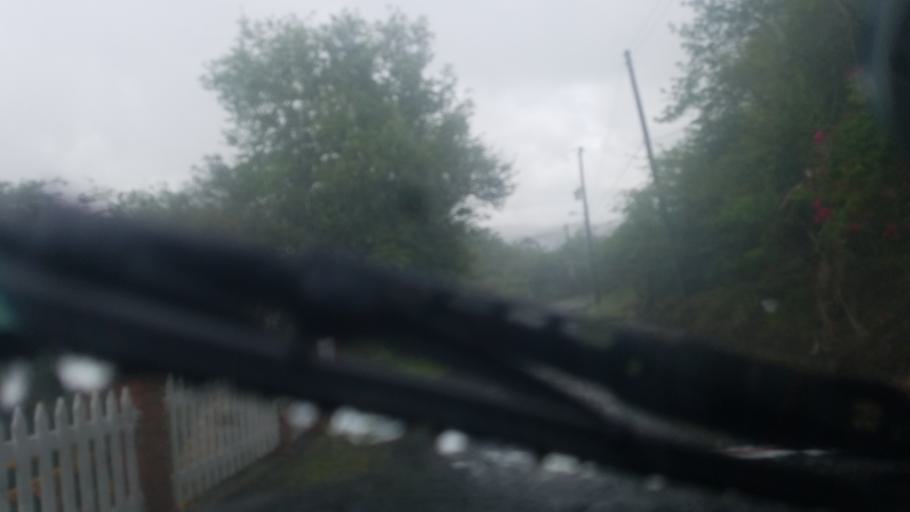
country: LC
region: Laborie Quarter
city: Laborie
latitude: 13.7422
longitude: -60.9686
